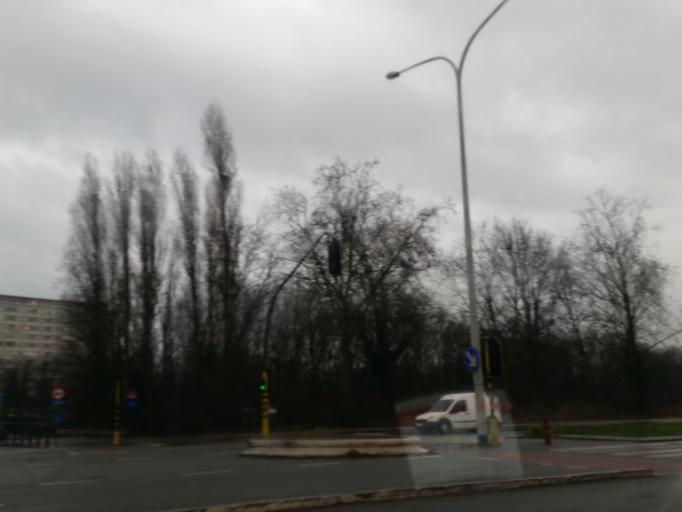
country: BE
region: Flanders
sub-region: Provincie Antwerpen
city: Antwerpen
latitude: 51.2035
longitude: 4.4370
